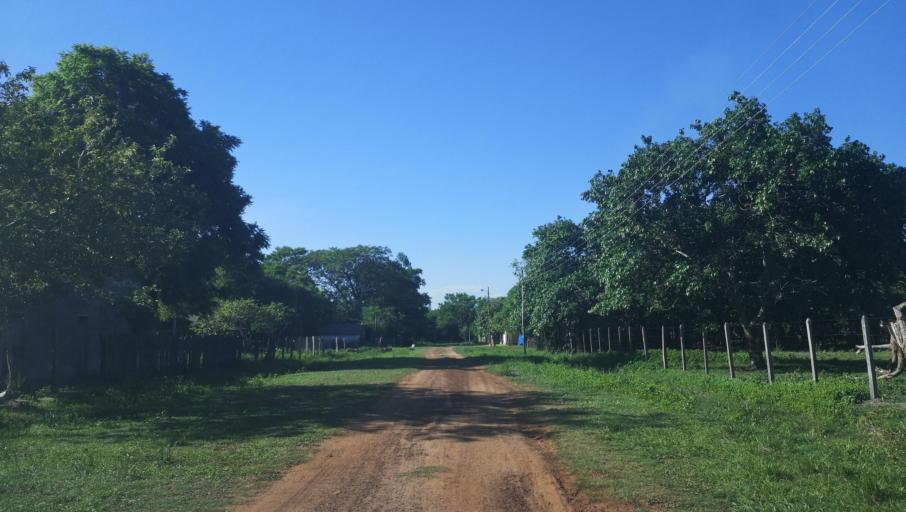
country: PY
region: Caaguazu
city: Carayao
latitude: -25.1935
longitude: -56.4004
